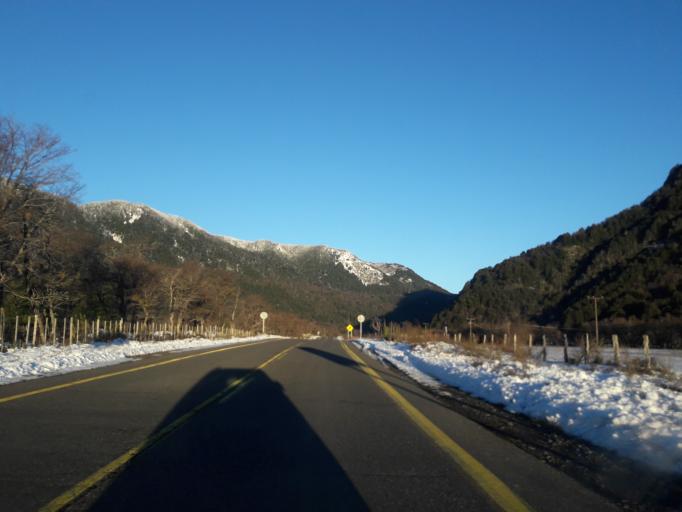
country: CL
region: Araucania
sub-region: Provincia de Cautin
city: Vilcun
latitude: -38.4825
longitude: -71.5348
